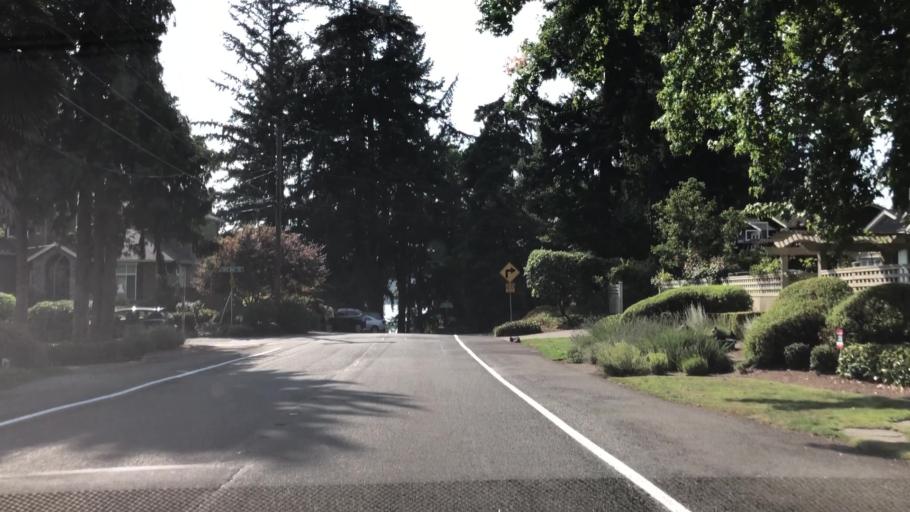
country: US
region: Washington
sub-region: King County
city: Bellevue
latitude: 47.5881
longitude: -122.2036
